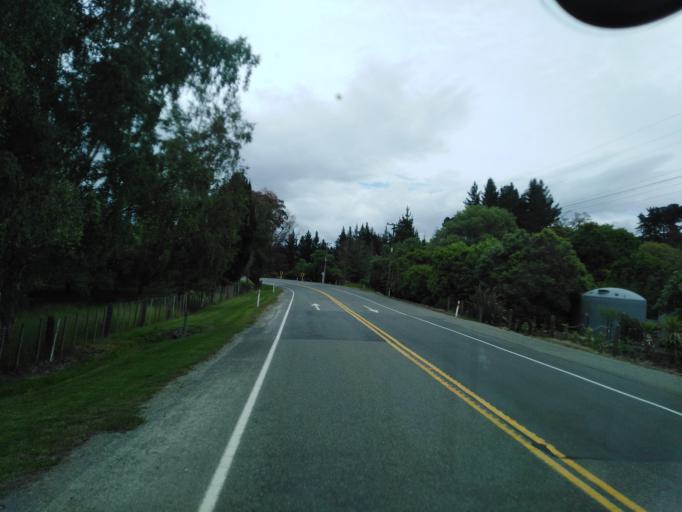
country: NZ
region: Tasman
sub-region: Tasman District
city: Wakefield
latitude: -41.4499
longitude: 172.9590
